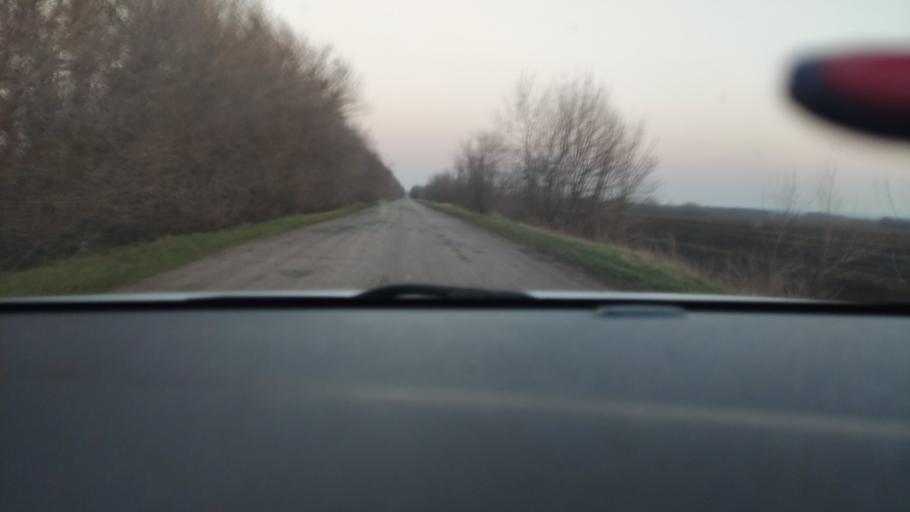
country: RU
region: Voronezj
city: Uryv-Pokrovka
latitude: 51.1362
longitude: 39.0871
